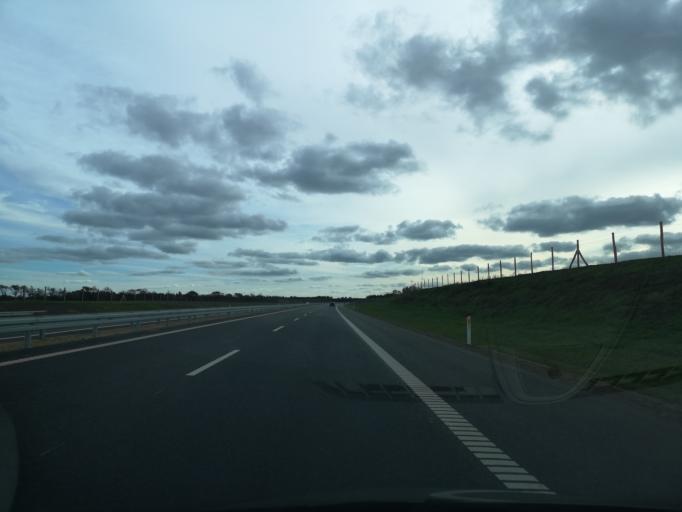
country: DK
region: Central Jutland
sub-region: Herning Kommune
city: Avlum
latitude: 56.3447
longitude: 8.7378
